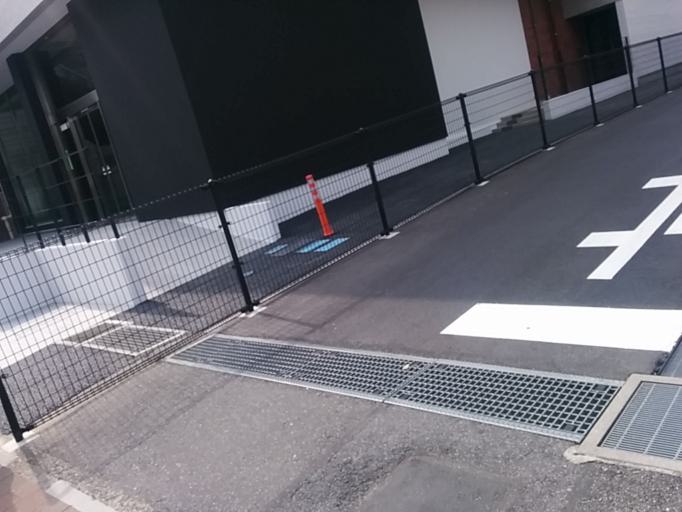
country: JP
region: Tokyo
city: Urayasu
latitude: 35.6673
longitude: 139.8600
